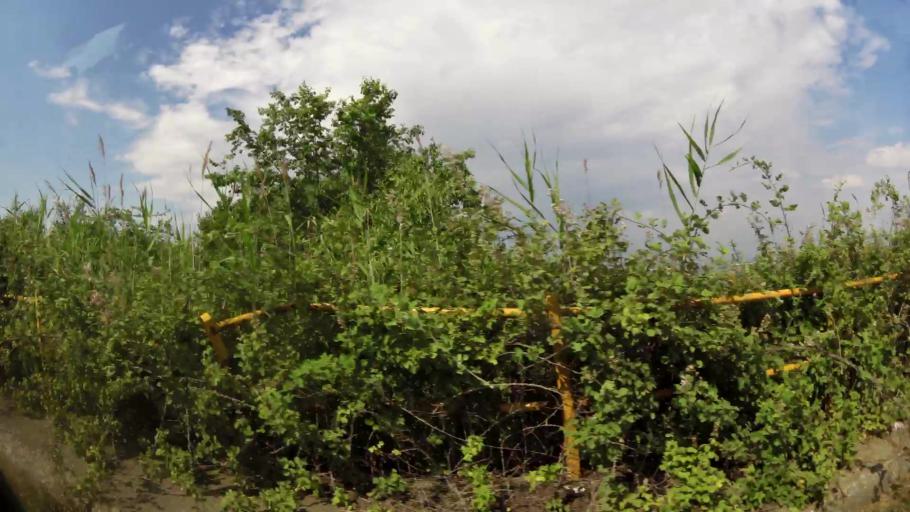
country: GR
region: Central Macedonia
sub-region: Nomos Pierias
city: Makrygialos
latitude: 40.3769
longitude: 22.6234
